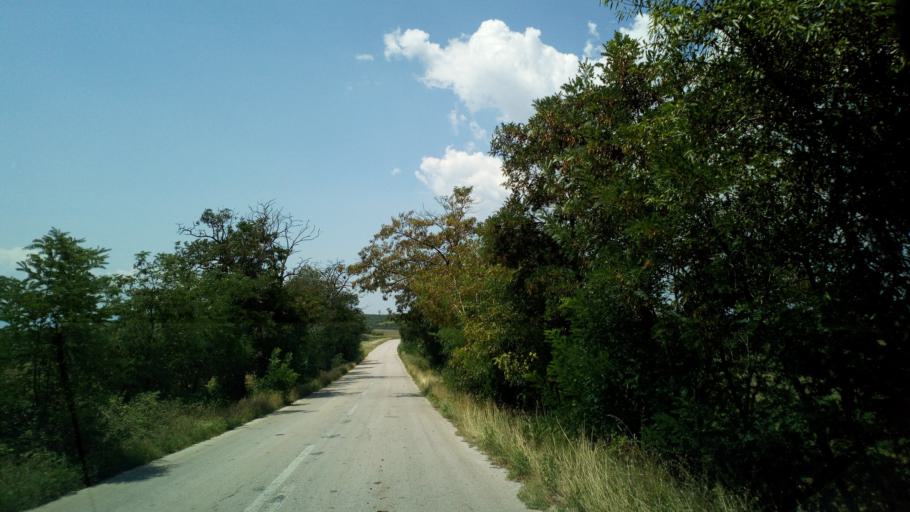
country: GR
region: Central Macedonia
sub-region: Nomos Thessalonikis
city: Askos
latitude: 40.7380
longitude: 23.3801
